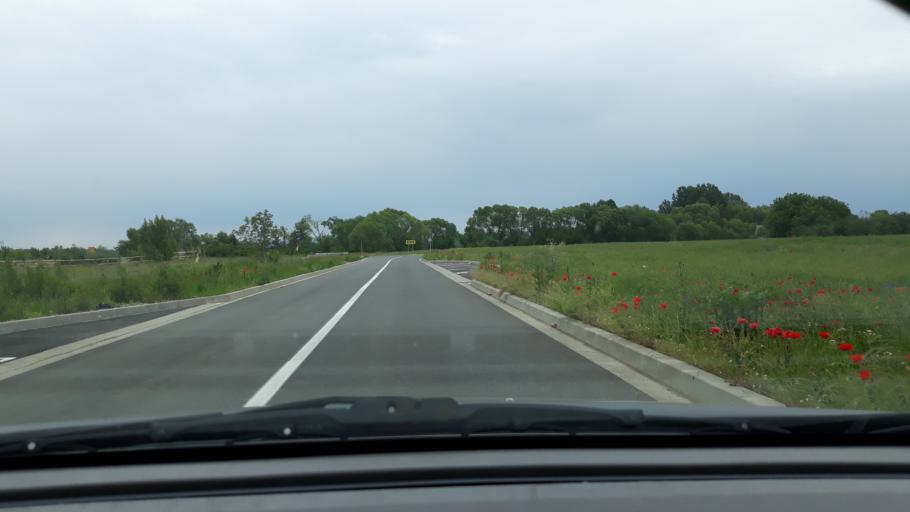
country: RO
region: Bihor
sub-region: Comuna Osorheiu
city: Osorheiu
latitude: 47.0661
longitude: 22.0380
